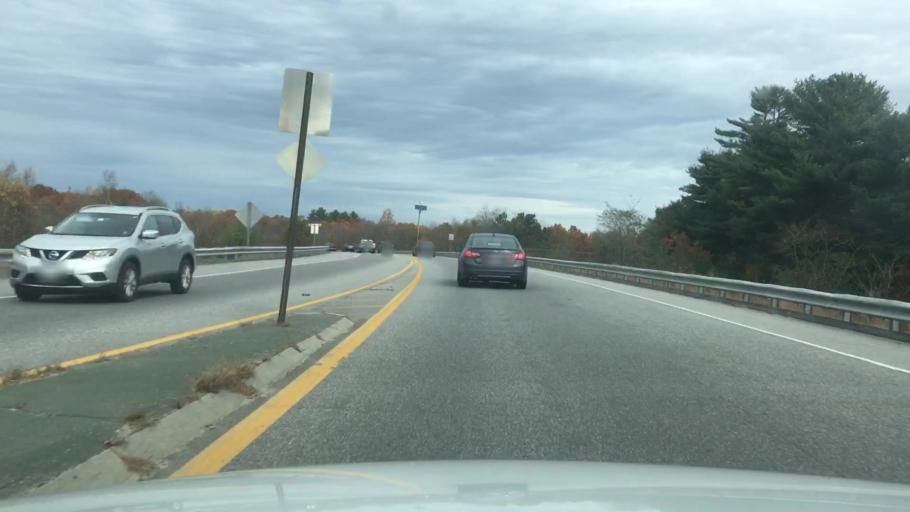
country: US
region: Maine
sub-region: Cumberland County
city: Brunswick
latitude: 43.9300
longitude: -69.9488
